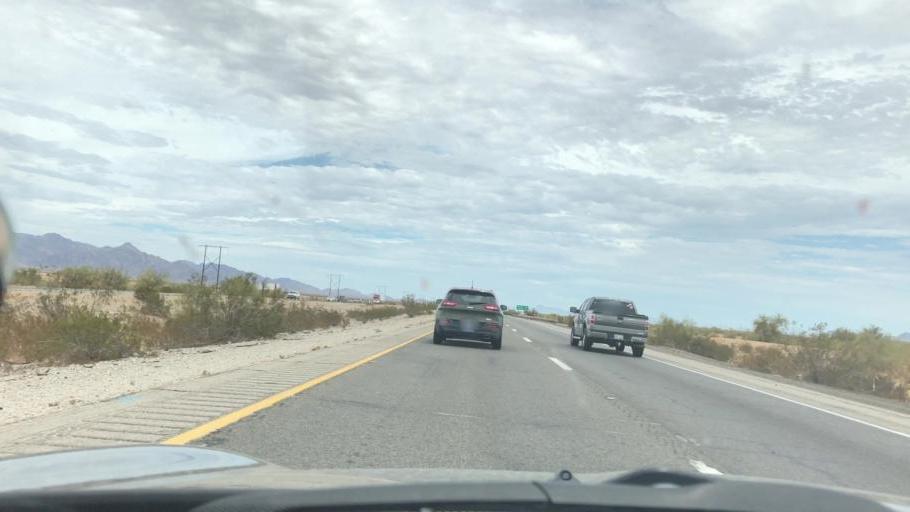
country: US
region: California
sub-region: Riverside County
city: Mesa Verde
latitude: 33.6058
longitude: -114.9764
